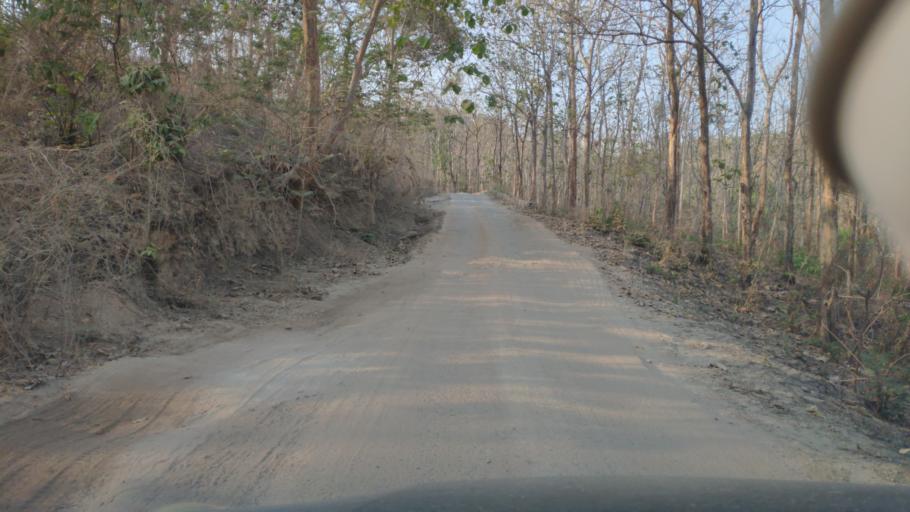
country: ID
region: Central Java
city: Sendangrejo
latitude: -6.9149
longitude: 111.5549
